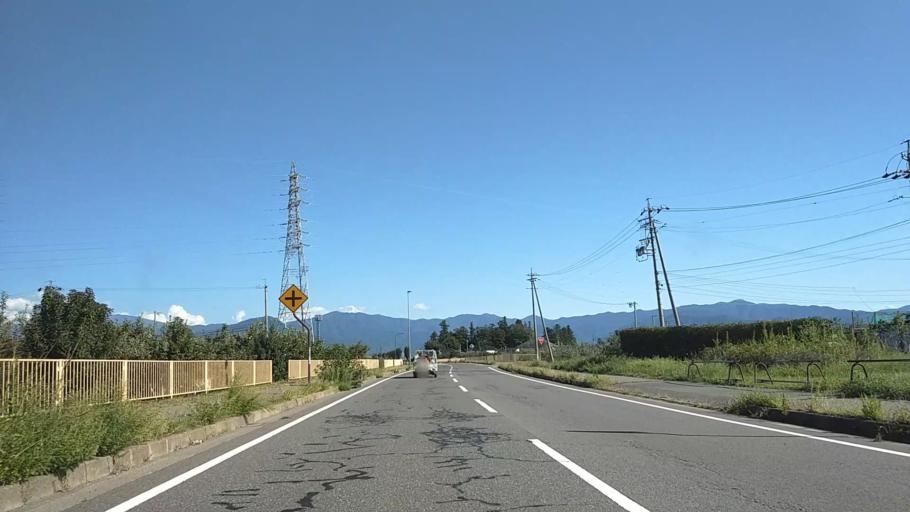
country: JP
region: Nagano
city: Nagano-shi
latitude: 36.6152
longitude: 138.1375
